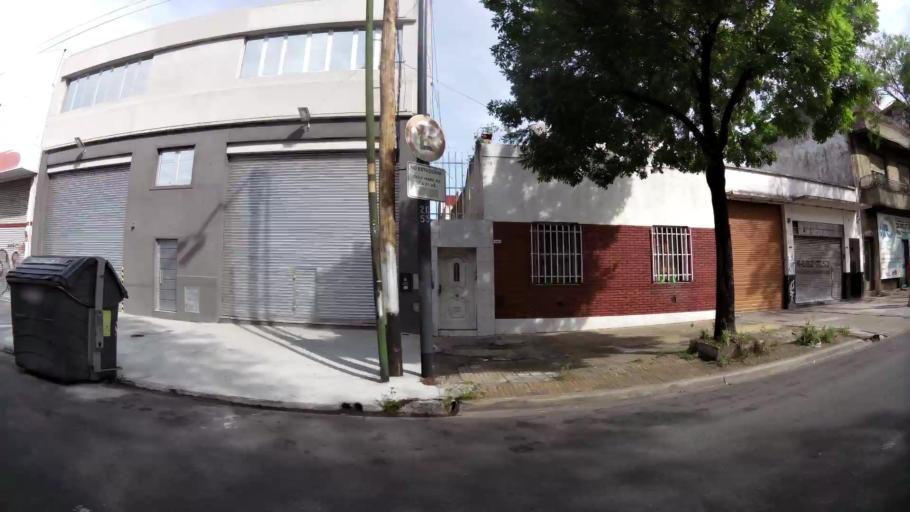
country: AR
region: Buenos Aires F.D.
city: Villa Lugano
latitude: -34.6546
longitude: -58.4953
